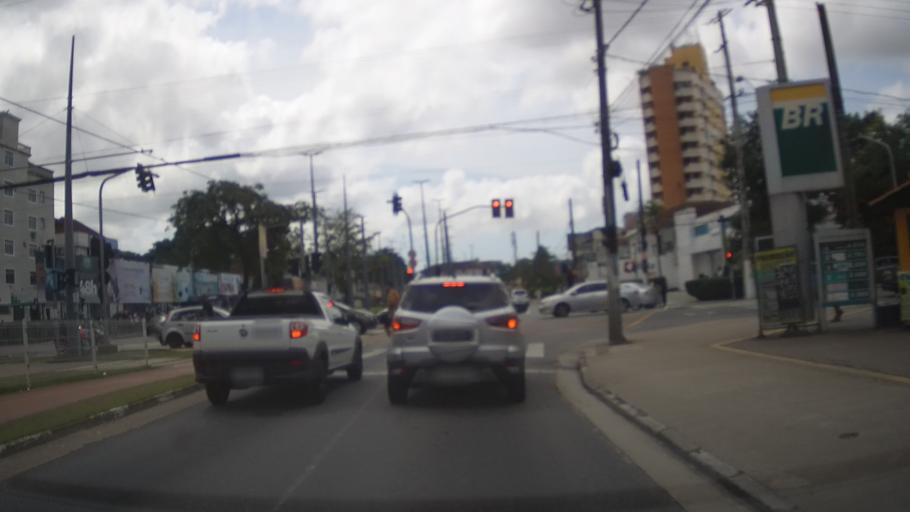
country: BR
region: Sao Paulo
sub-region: Santos
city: Santos
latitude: -23.9577
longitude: -46.3232
